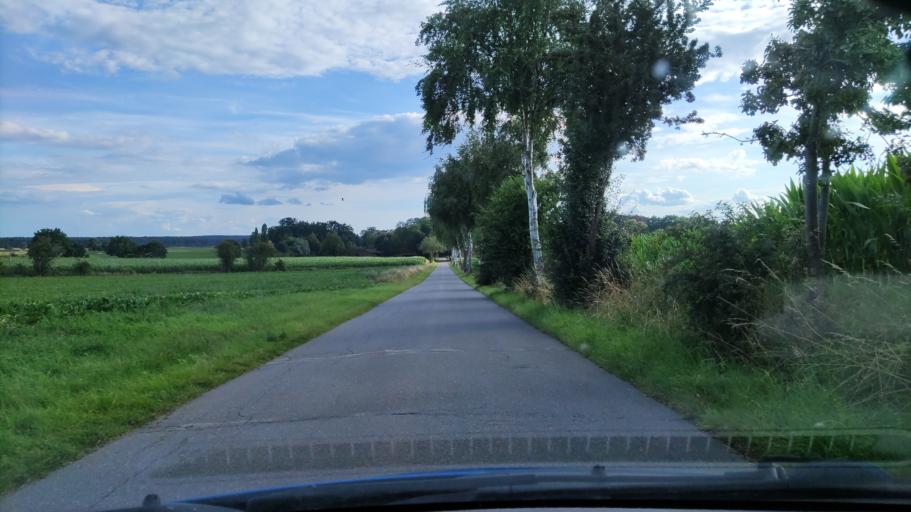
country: DE
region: Lower Saxony
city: Boitze
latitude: 53.1536
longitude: 10.7518
